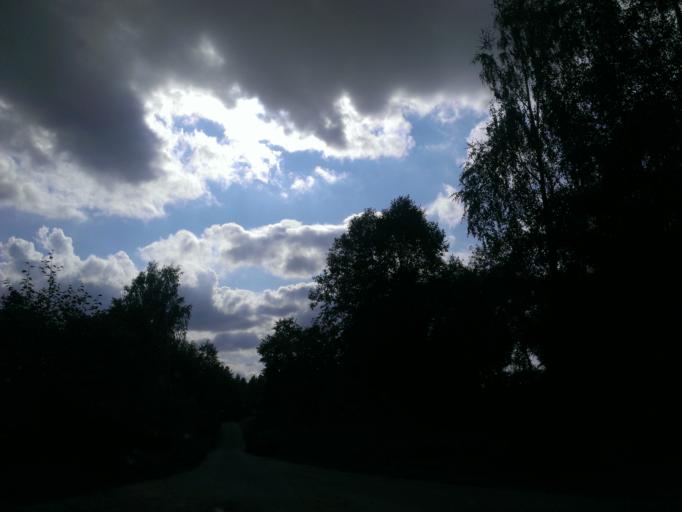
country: LV
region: Incukalns
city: Vangazi
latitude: 57.1041
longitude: 24.5268
